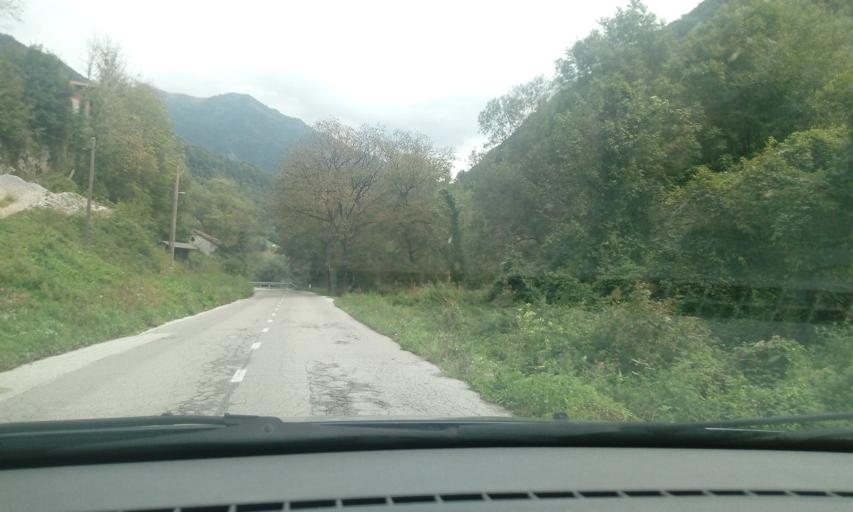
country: SI
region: Tolmin
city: Tolmin
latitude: 46.1513
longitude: 13.7716
